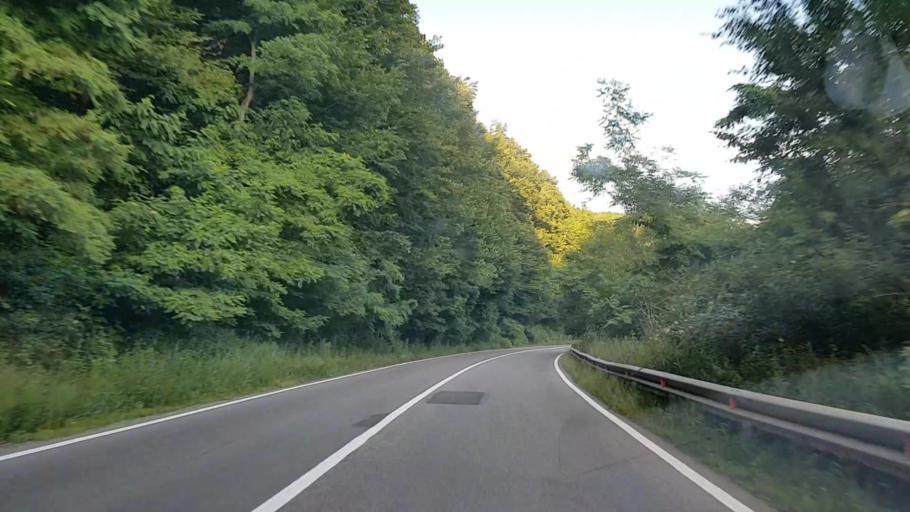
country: RO
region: Harghita
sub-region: Comuna Corund
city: Corund
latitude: 46.4495
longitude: 25.2223
